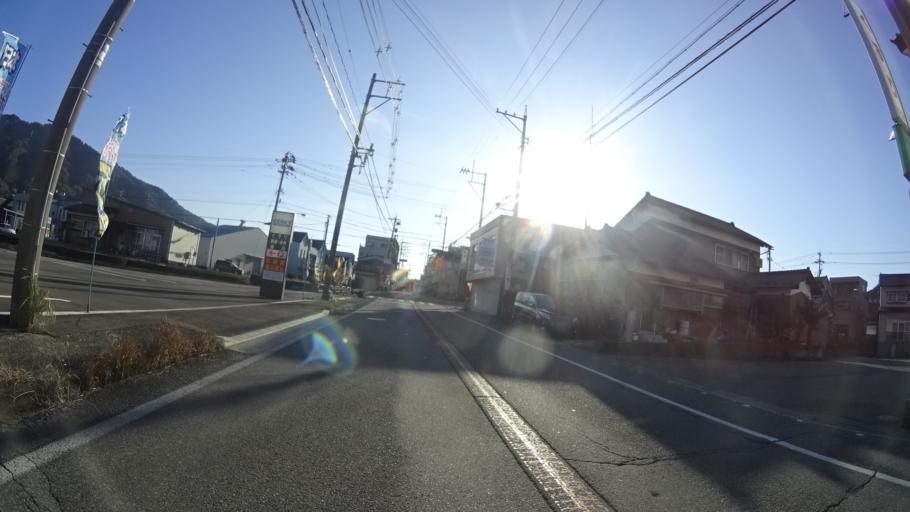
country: JP
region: Fukui
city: Maruoka
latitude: 36.0988
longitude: 136.3251
